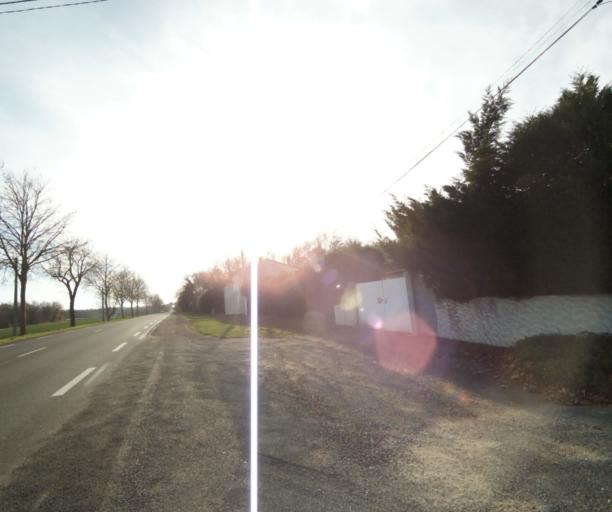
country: FR
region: Poitou-Charentes
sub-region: Departement de la Charente-Maritime
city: Saint-Hilaire-de-Villefranche
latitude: 45.8323
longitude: -0.5393
